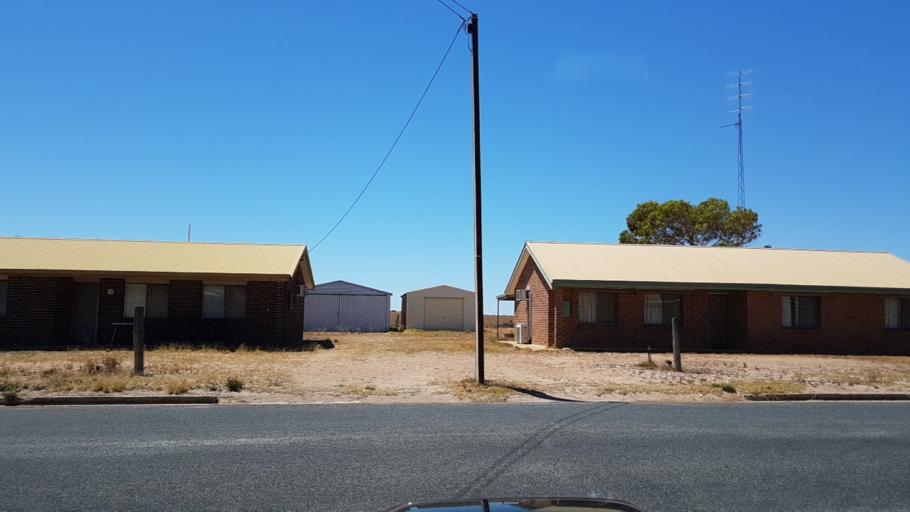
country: AU
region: South Australia
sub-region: Copper Coast
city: Wallaroo
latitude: -33.8985
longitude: 137.6300
